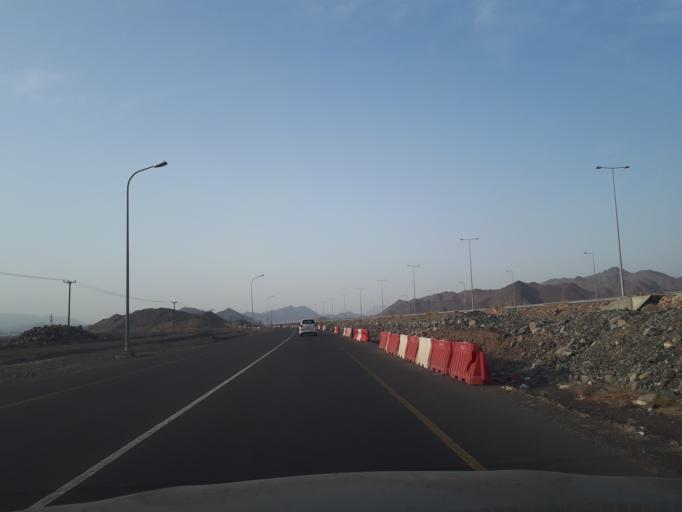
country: OM
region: Muhafazat ad Dakhiliyah
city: Sufalat Sama'il
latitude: 23.2777
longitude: 58.1067
